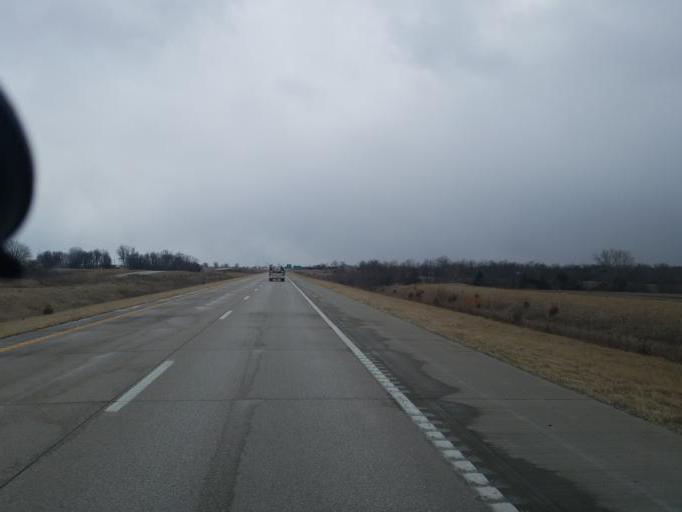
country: US
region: Missouri
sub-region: Randolph County
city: Moberly
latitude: 39.4751
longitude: -92.4348
